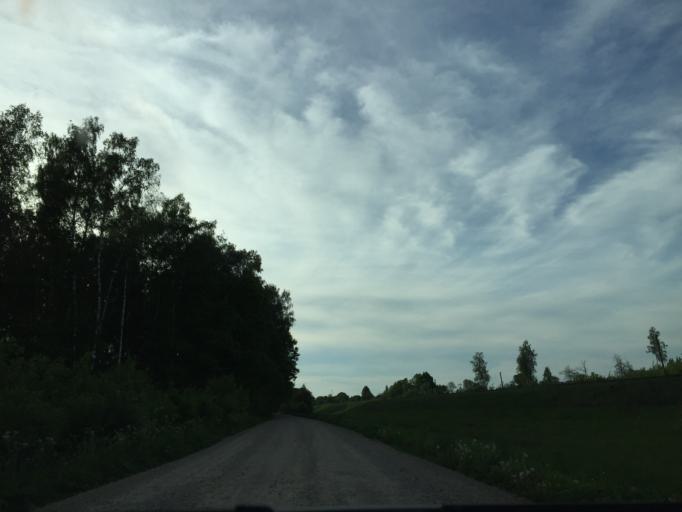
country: LV
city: Tireli
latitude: 56.6785
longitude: 23.5031
